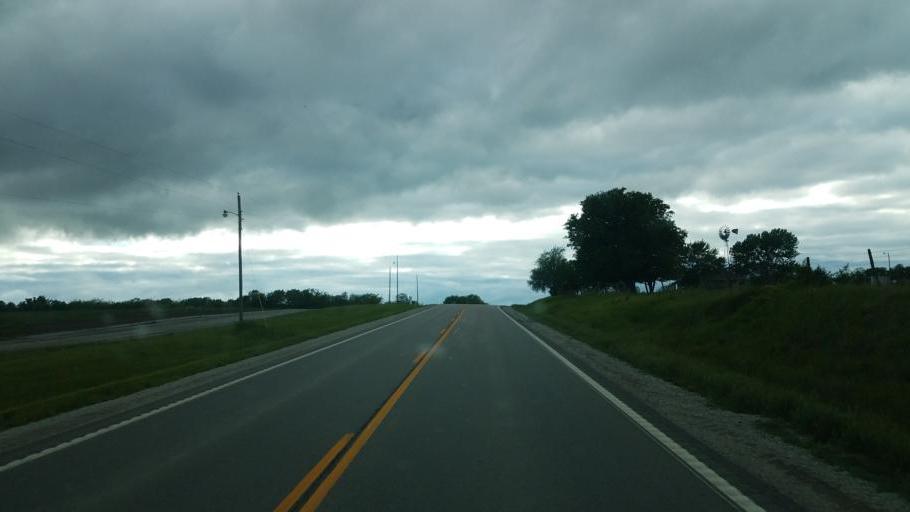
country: US
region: Missouri
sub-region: Harrison County
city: Bethany
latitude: 40.2647
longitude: -93.9849
